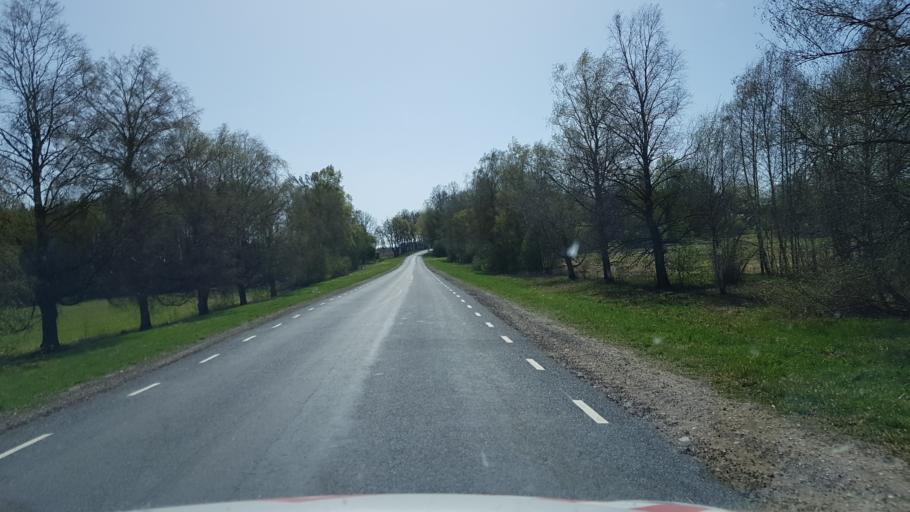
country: EE
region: Viljandimaa
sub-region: Vohma linn
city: Vohma
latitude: 58.5876
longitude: 25.5298
